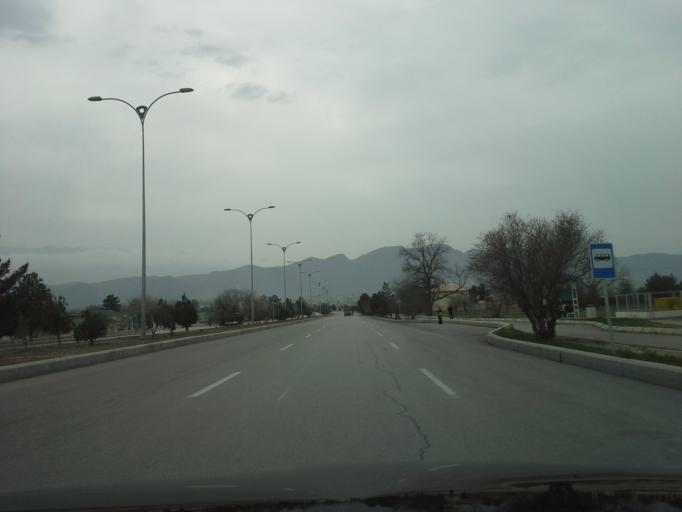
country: TM
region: Ahal
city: Abadan
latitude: 37.9710
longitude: 58.2349
